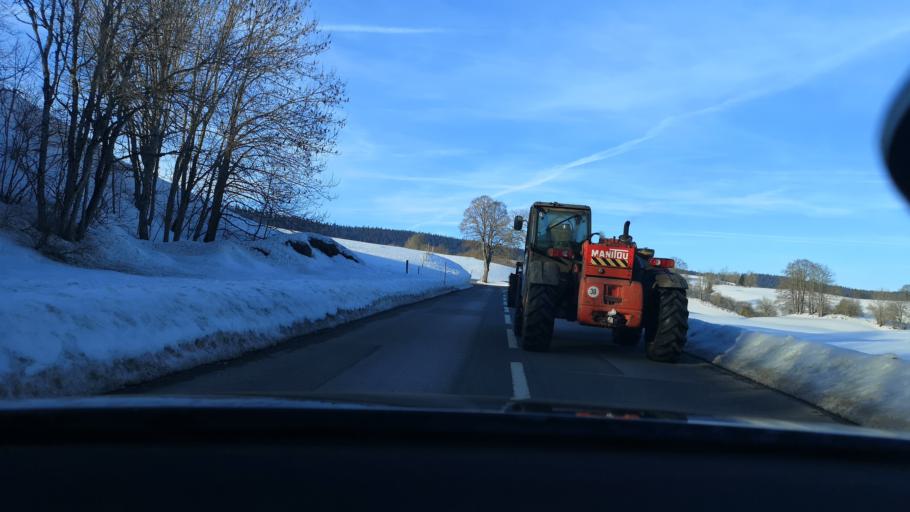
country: CH
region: Neuchatel
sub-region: Val-de-Travers District
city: Fleurier
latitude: 46.9076
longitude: 6.4999
